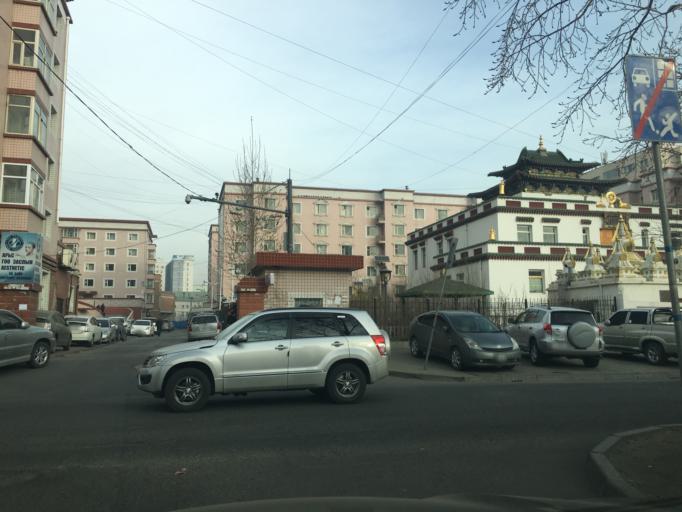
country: MN
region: Ulaanbaatar
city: Ulaanbaatar
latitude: 47.9125
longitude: 106.8850
